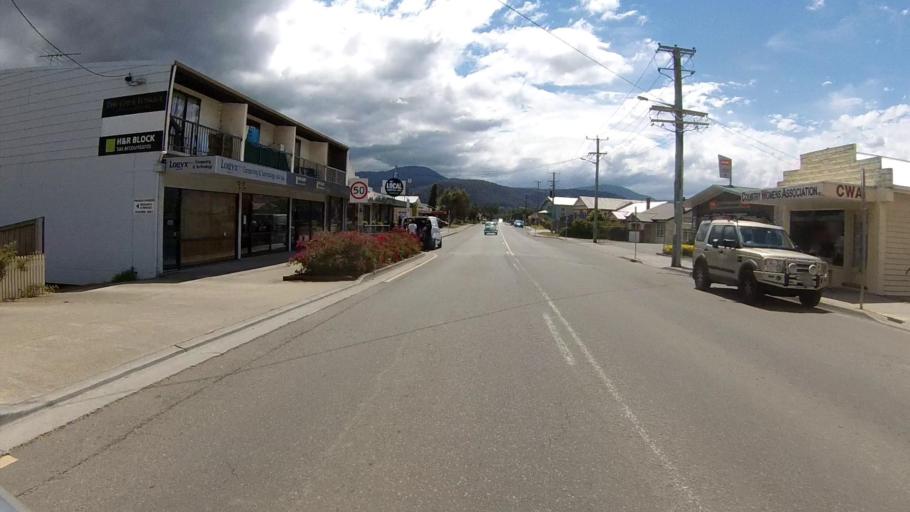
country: AU
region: Tasmania
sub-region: Huon Valley
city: Huonville
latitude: -43.0304
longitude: 147.0479
